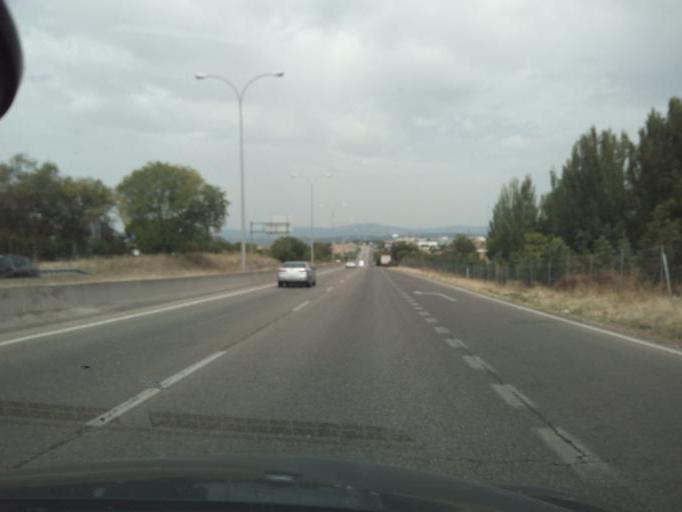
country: ES
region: Madrid
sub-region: Provincia de Madrid
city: Las Rozas de Madrid
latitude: 40.4924
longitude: -3.8800
